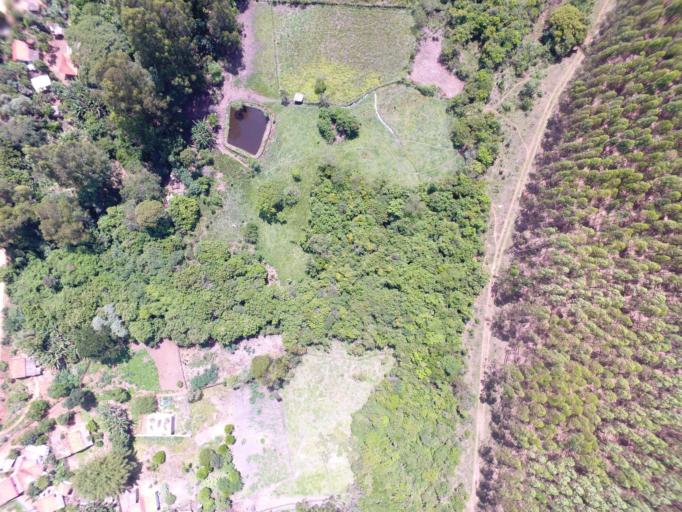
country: BR
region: Minas Gerais
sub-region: Barroso
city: Barroso
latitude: -21.0409
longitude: -43.9999
